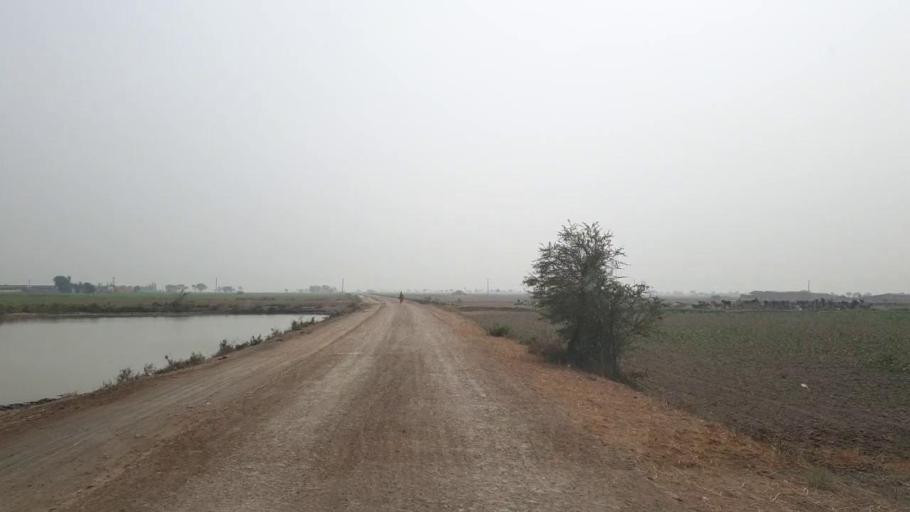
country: PK
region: Sindh
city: Kario
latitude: 24.6502
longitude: 68.5954
